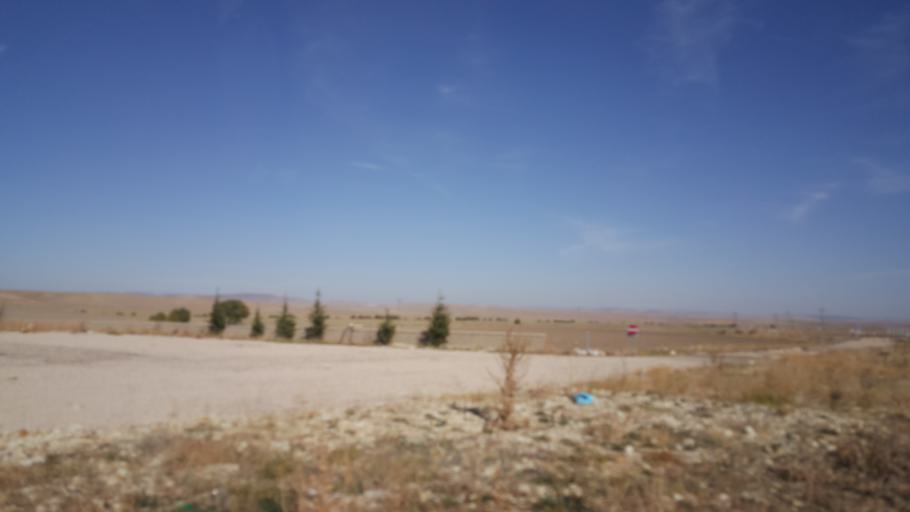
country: TR
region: Ankara
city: Yenice
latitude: 39.3733
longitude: 32.7261
